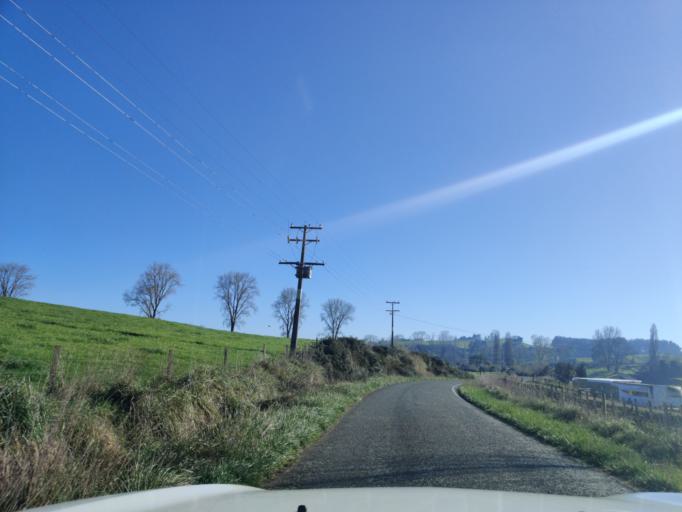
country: NZ
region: Waikato
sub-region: Matamata-Piako District
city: Matamata
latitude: -37.9912
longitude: 175.7162
